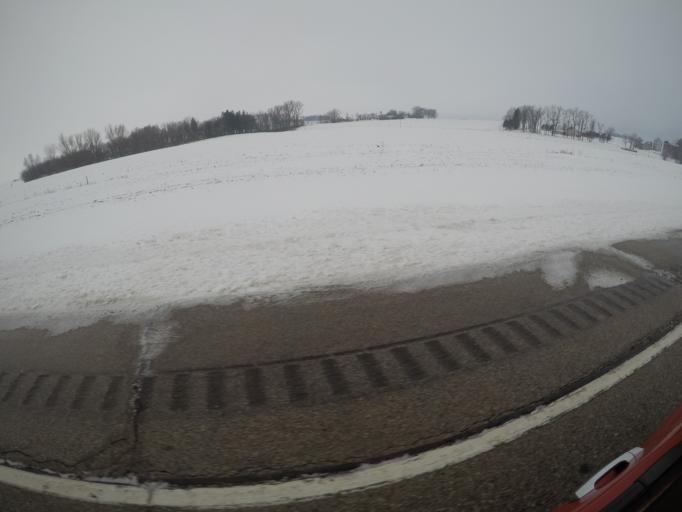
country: US
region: Minnesota
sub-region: Goodhue County
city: Wanamingo
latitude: 44.3942
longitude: -92.8372
